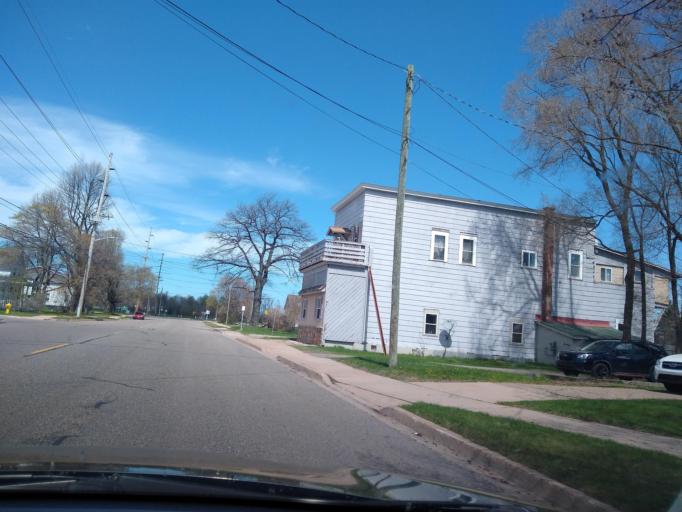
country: US
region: Michigan
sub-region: Marquette County
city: Marquette
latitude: 46.5695
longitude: -87.3961
